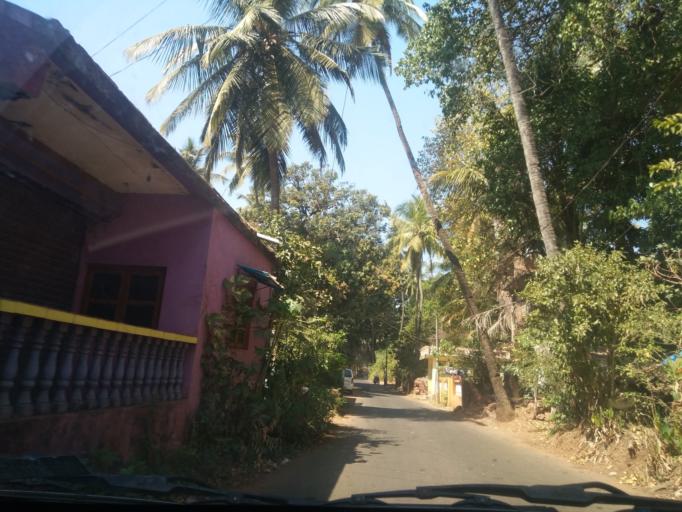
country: IN
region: Goa
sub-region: North Goa
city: Morjim
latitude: 15.6339
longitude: 73.7416
